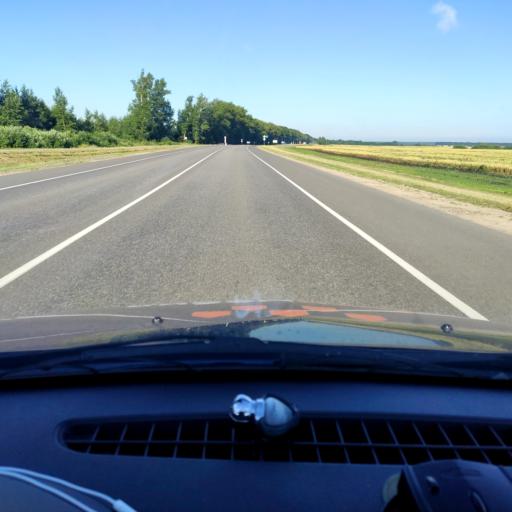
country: RU
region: Orjol
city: Pokrovskoye
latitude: 52.6213
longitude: 36.7697
